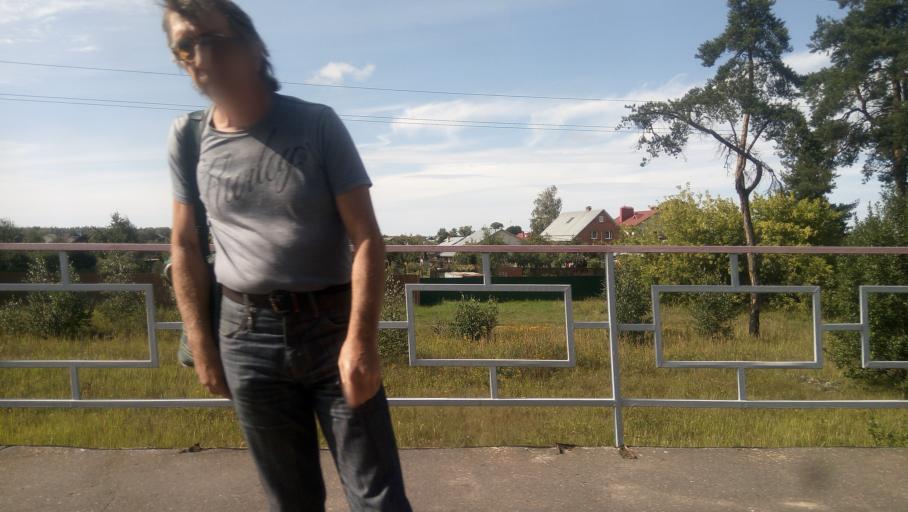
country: RU
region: Moskovskaya
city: Vereya
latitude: 55.8434
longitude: 39.0642
